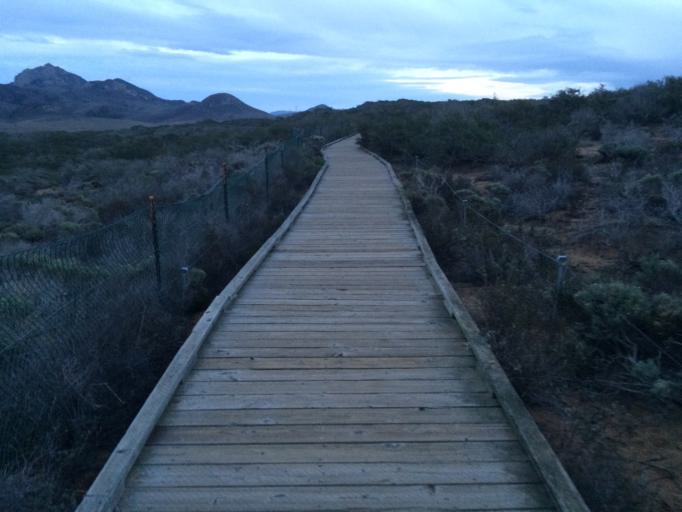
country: US
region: California
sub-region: San Luis Obispo County
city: Los Osos
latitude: 35.3331
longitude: -120.8291
